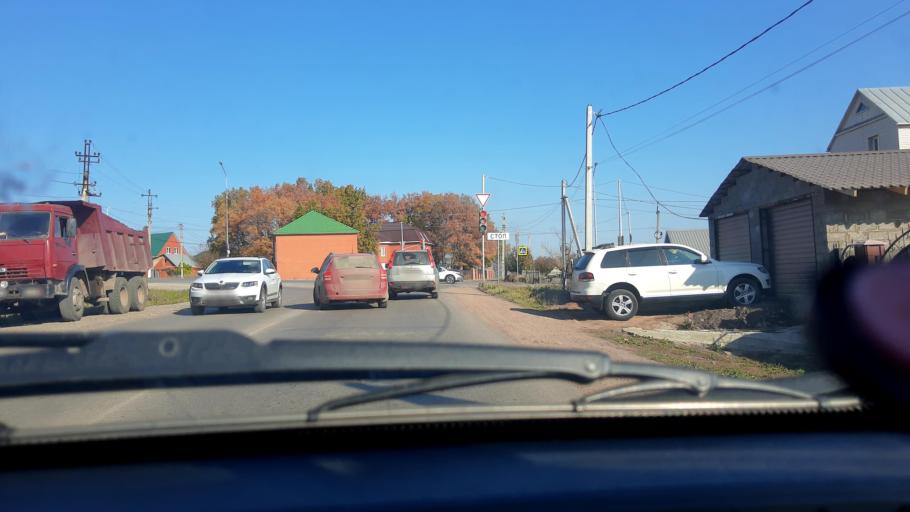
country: RU
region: Bashkortostan
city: Mikhaylovka
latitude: 54.8139
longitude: 55.8842
